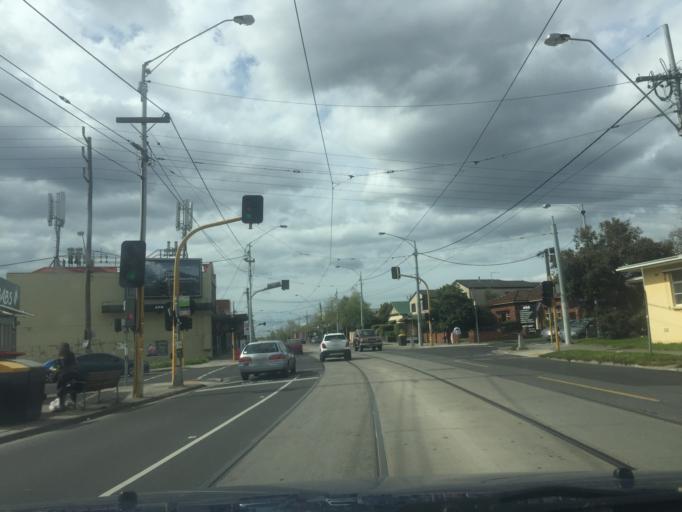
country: AU
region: Victoria
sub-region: Darebin
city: Preston
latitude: -37.7393
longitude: 145.0112
